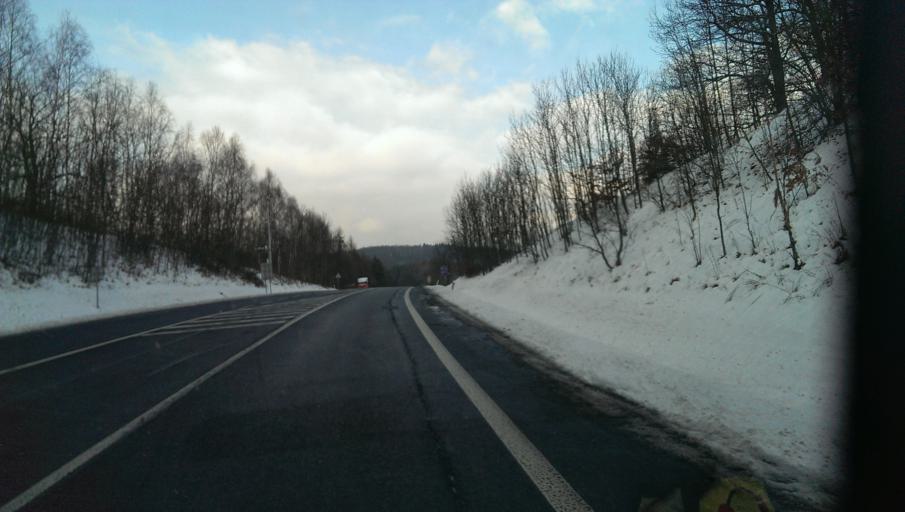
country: CZ
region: Ustecky
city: Velemin
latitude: 50.5662
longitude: 13.9581
